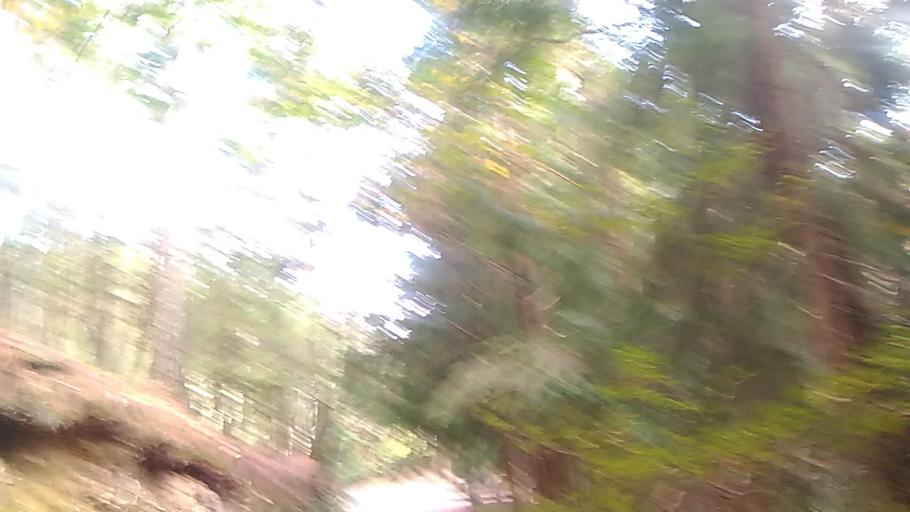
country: TW
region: Taiwan
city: Daxi
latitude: 24.4038
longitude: 121.3059
